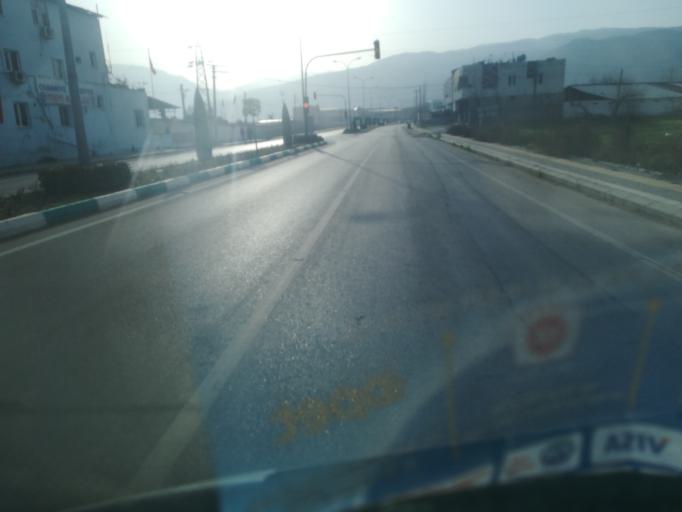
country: TR
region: Osmaniye
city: Osmaniye
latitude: 37.0573
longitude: 36.2191
